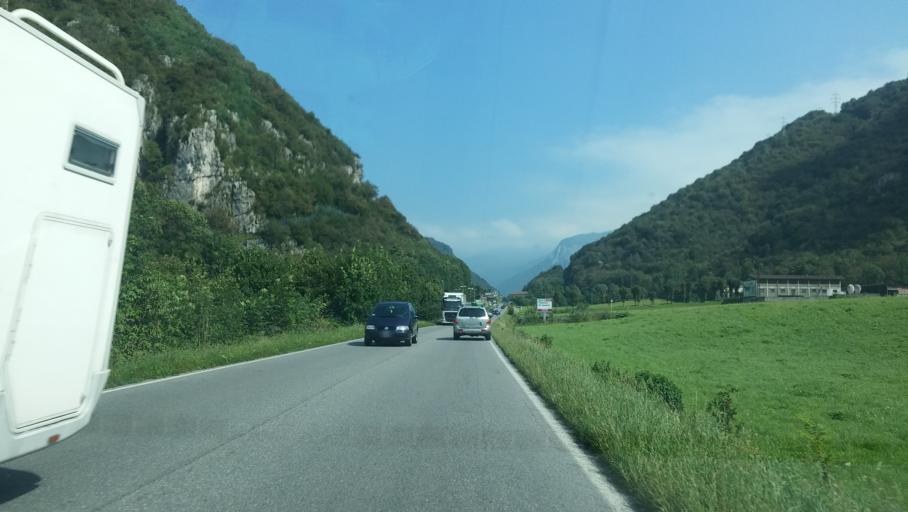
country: IT
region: Lombardy
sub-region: Provincia di Lecco
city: Ballabio
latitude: 45.9131
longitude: 9.4326
